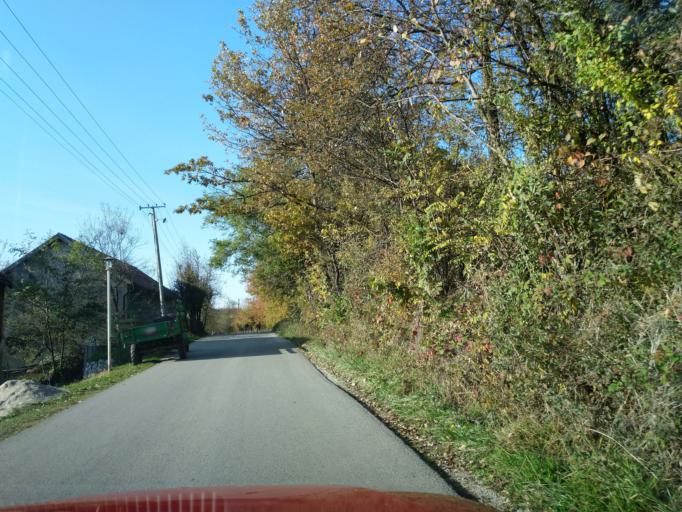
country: RS
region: Central Serbia
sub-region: Zlatiborski Okrug
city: Uzice
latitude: 43.8694
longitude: 19.7577
